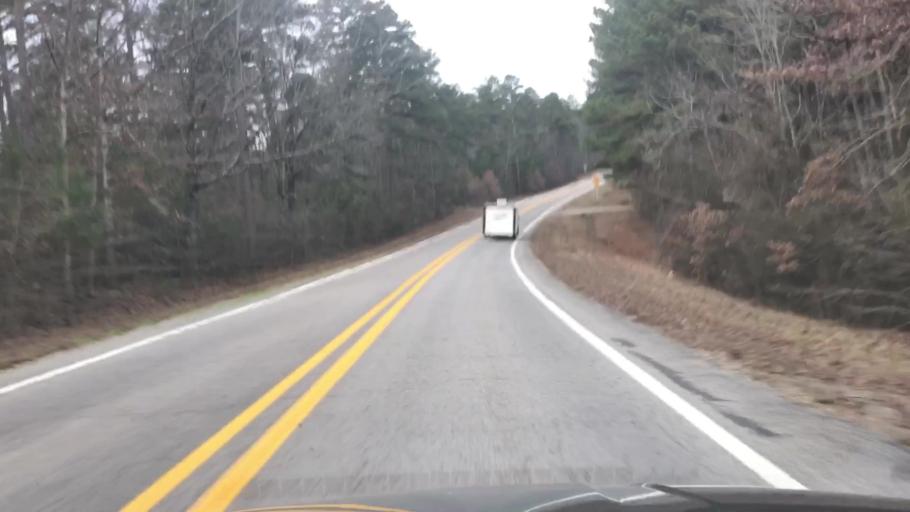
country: US
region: Arkansas
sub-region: Montgomery County
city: Mount Ida
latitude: 34.6715
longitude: -93.7826
